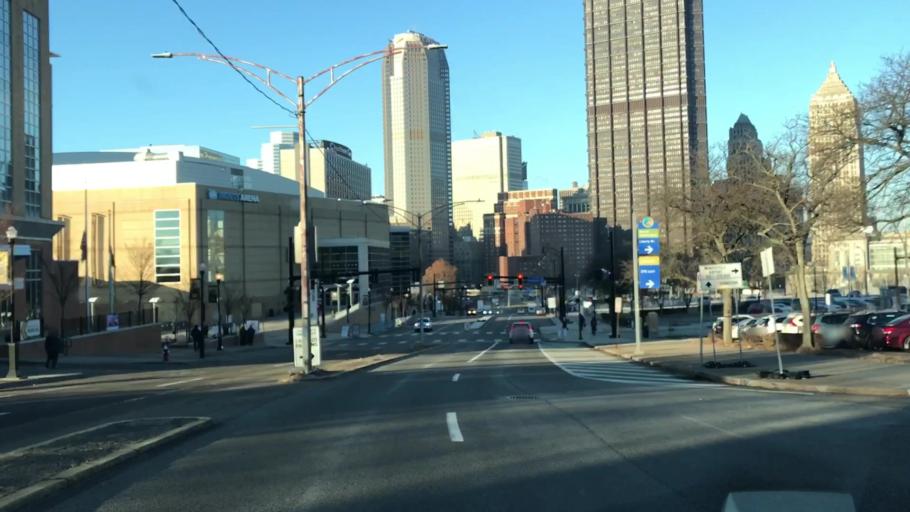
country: US
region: Pennsylvania
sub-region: Allegheny County
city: Pittsburgh
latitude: 40.4405
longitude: -79.9875
